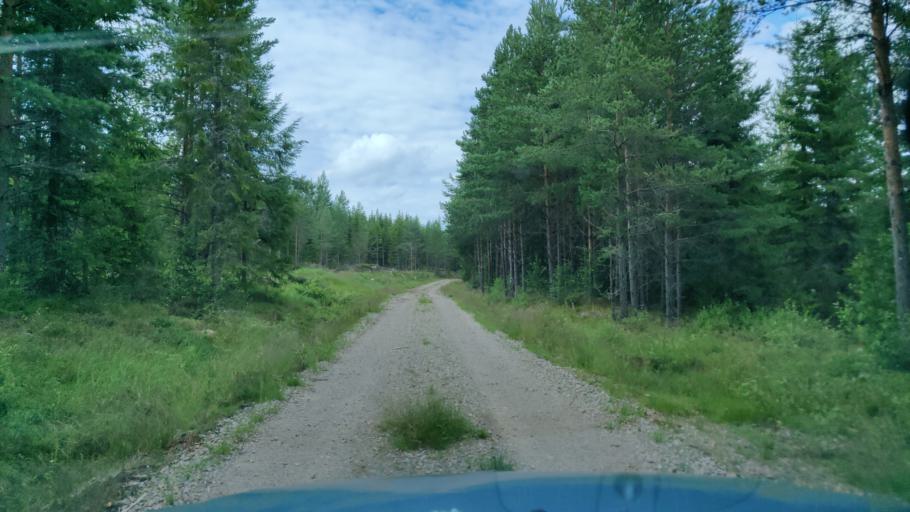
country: SE
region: Vaermland
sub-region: Hagfors Kommun
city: Hagfors
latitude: 59.9543
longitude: 13.5909
